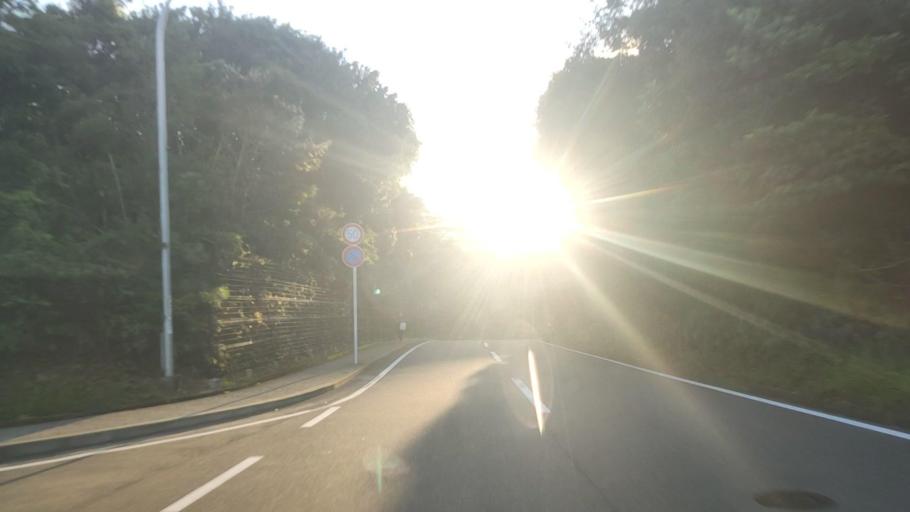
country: JP
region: Mie
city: Toba
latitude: 34.3099
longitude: 136.8181
